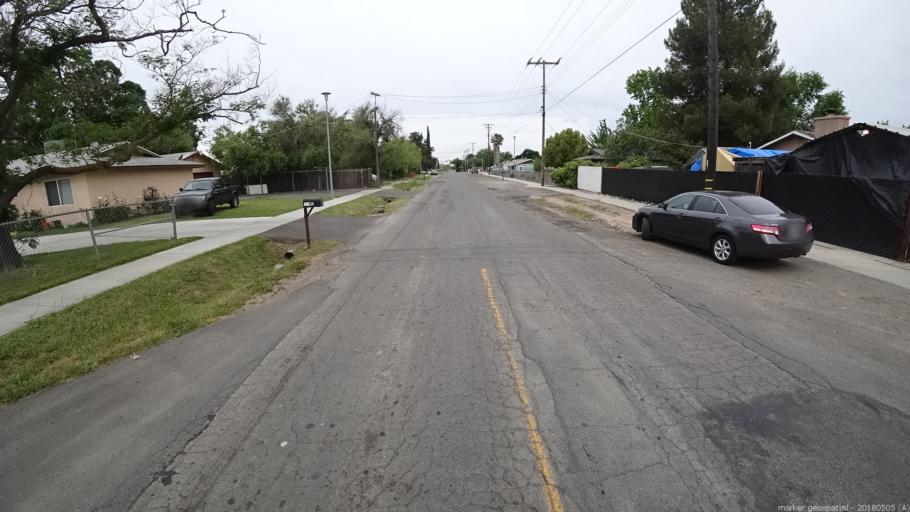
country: US
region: California
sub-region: Sacramento County
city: Rio Linda
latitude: 38.6547
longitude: -121.4386
